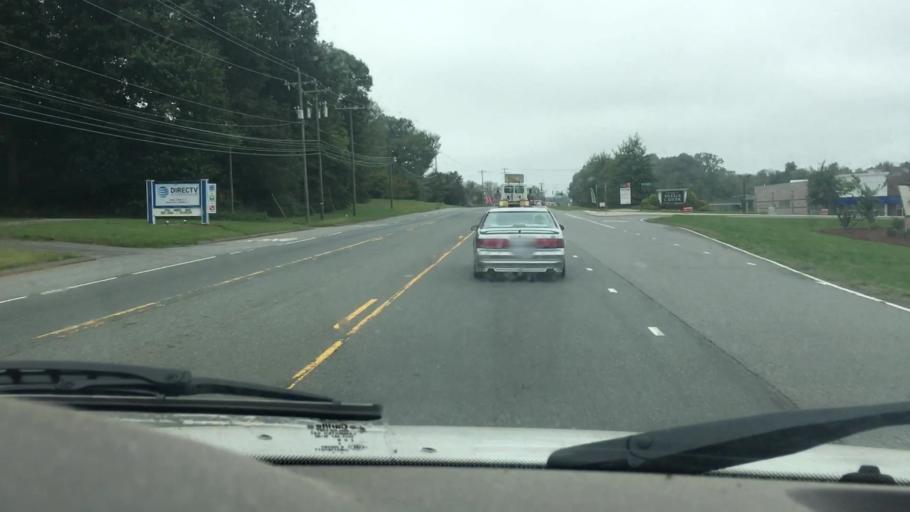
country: US
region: North Carolina
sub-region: Catawba County
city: Lake Norman of Catawba
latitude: 35.6005
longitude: -80.8937
